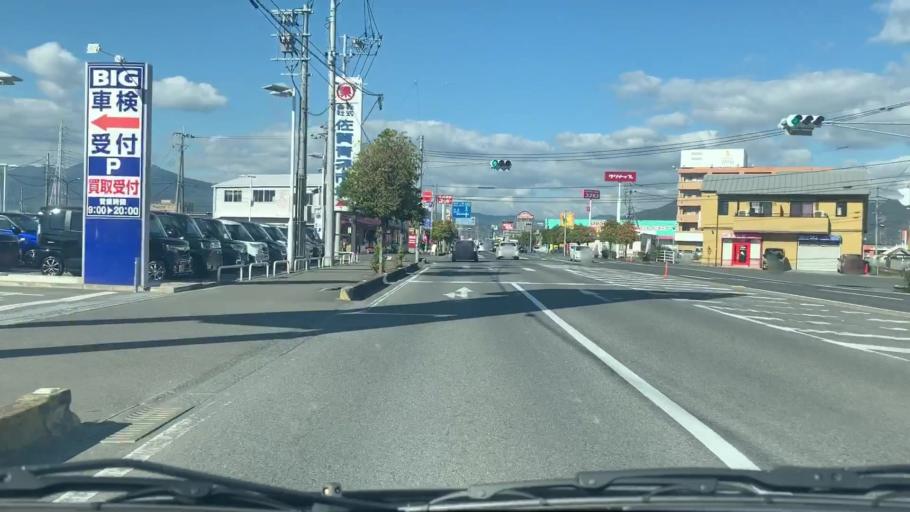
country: JP
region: Saga Prefecture
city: Saga-shi
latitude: 33.2903
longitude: 130.2869
